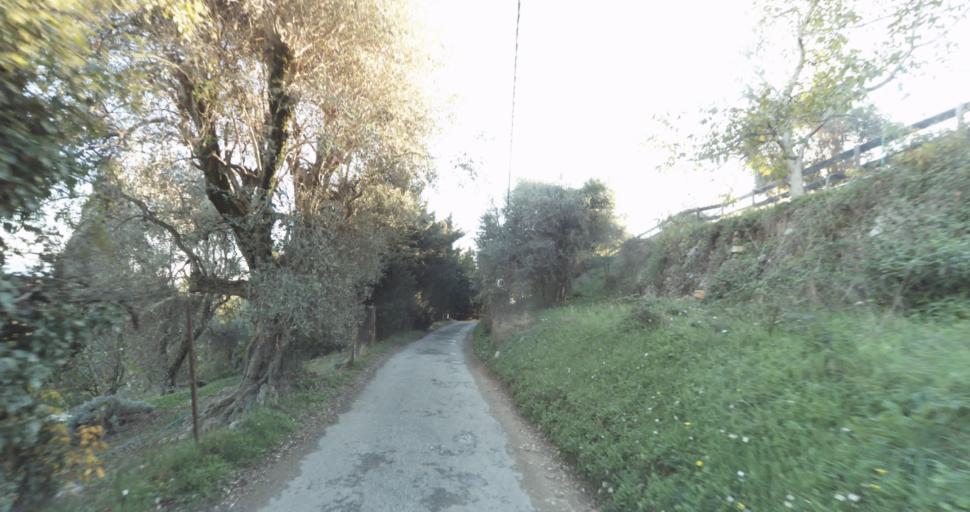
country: FR
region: Provence-Alpes-Cote d'Azur
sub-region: Departement des Alpes-Maritimes
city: Saint-Jeannet
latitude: 43.7410
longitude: 7.1287
